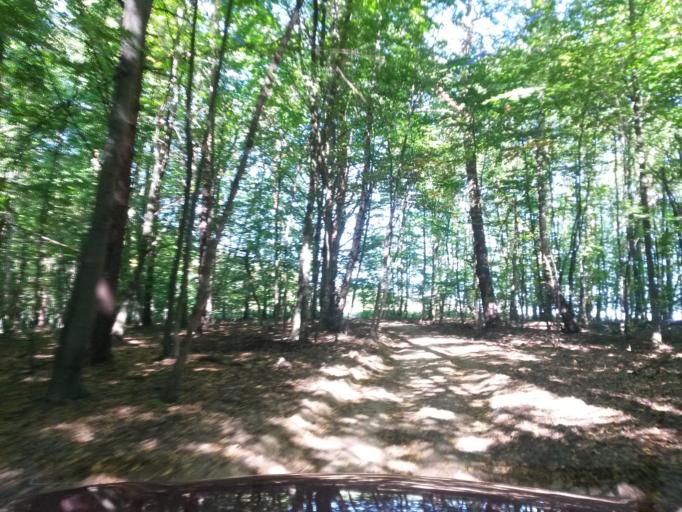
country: SK
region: Presovsky
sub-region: Okres Presov
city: Presov
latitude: 48.9830
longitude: 21.1473
